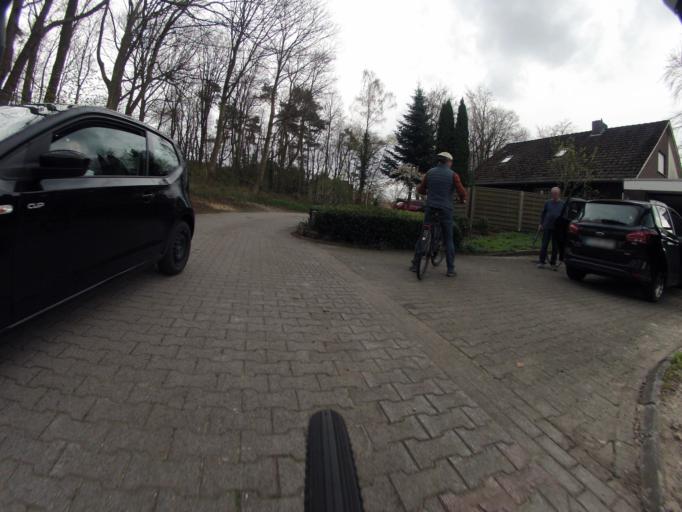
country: DE
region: North Rhine-Westphalia
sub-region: Regierungsbezirk Munster
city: Tecklenburg
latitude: 52.2577
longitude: 7.7839
